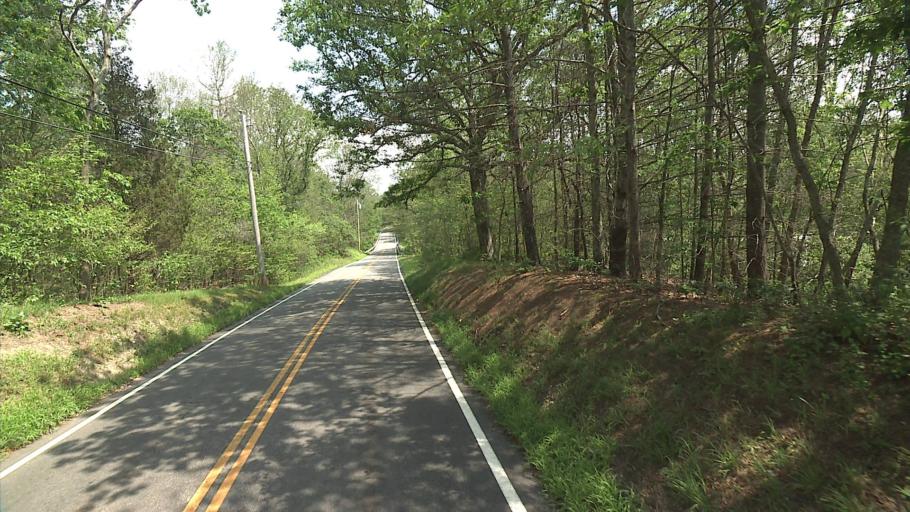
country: US
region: Connecticut
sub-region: Windham County
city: Moosup
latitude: 41.7582
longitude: -71.8516
